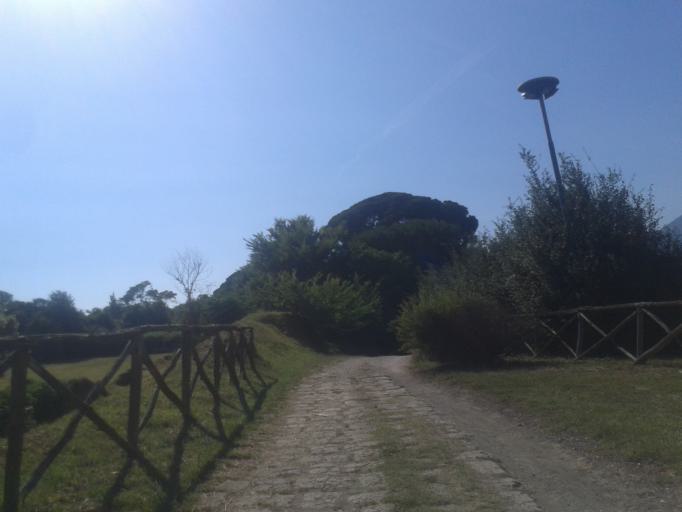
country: IT
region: Campania
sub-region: Provincia di Napoli
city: Pompei
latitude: 40.7531
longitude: 14.4940
